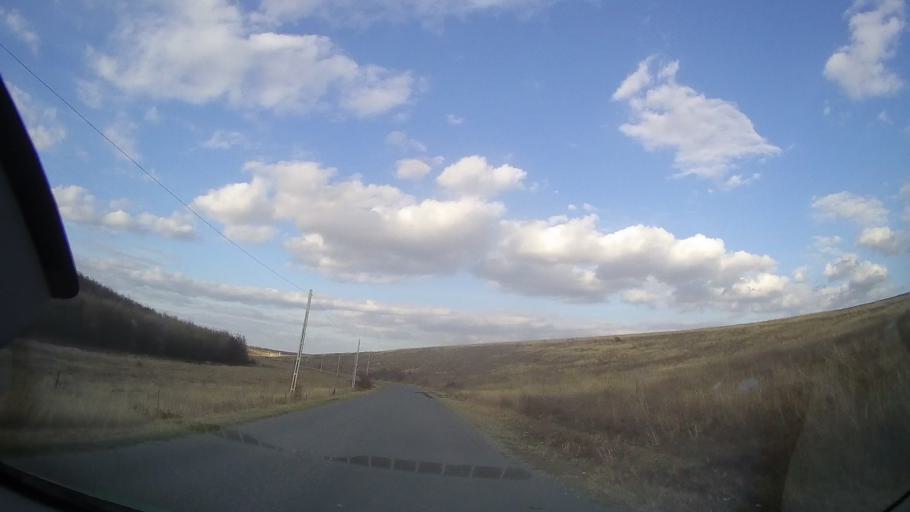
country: RO
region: Constanta
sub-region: Comuna Cerchezu
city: Cerchezu
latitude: 43.8338
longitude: 28.0969
